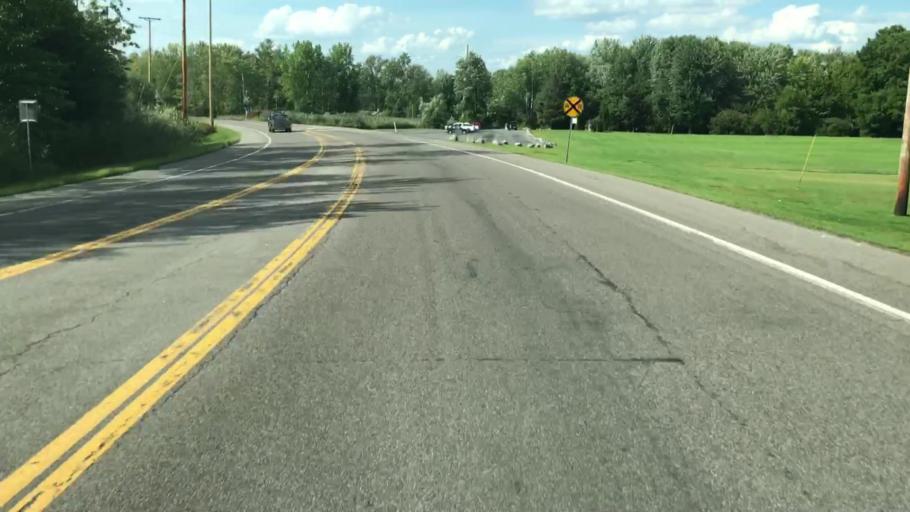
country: US
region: New York
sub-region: Onondaga County
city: Liverpool
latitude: 43.1514
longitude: -76.1883
